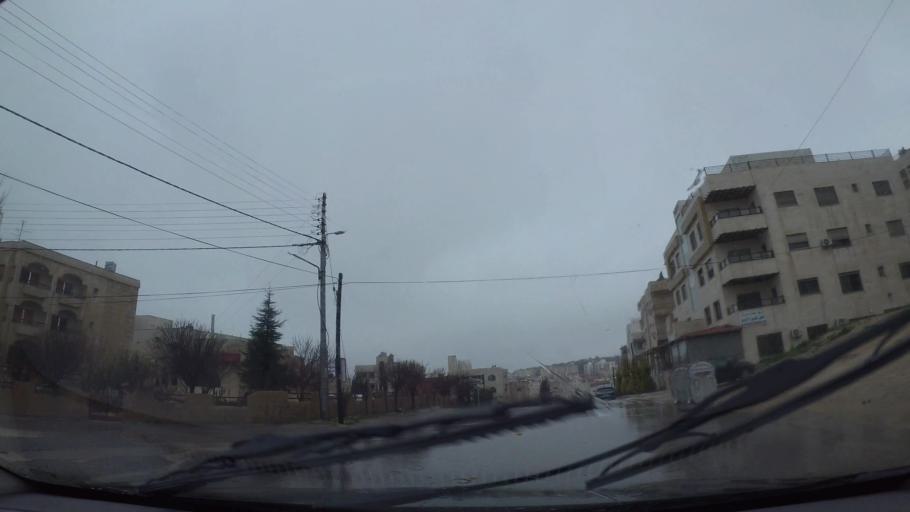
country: JO
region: Amman
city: Al Jubayhah
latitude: 32.0176
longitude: 35.8832
